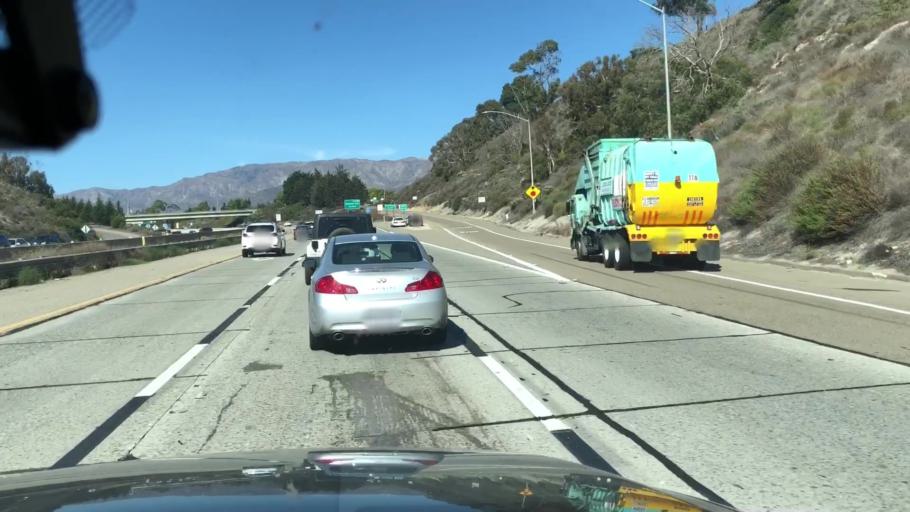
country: US
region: California
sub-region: Santa Barbara County
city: Carpinteria
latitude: 34.3810
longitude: -119.4820
